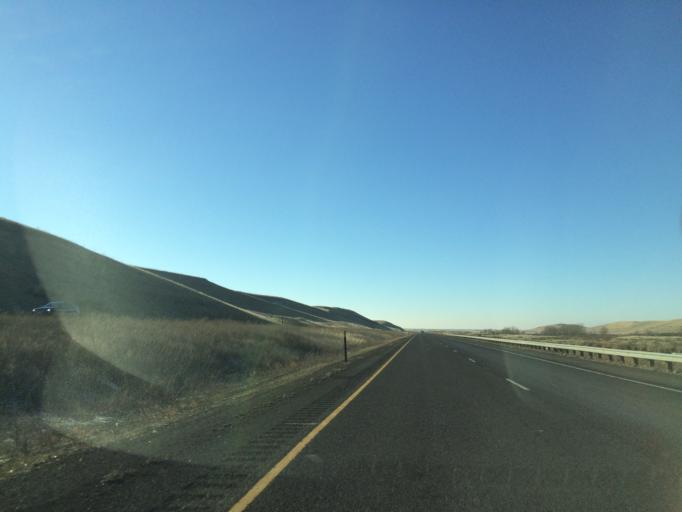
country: US
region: Washington
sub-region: Spokane County
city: Medical Lake
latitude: 47.3633
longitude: -117.8875
